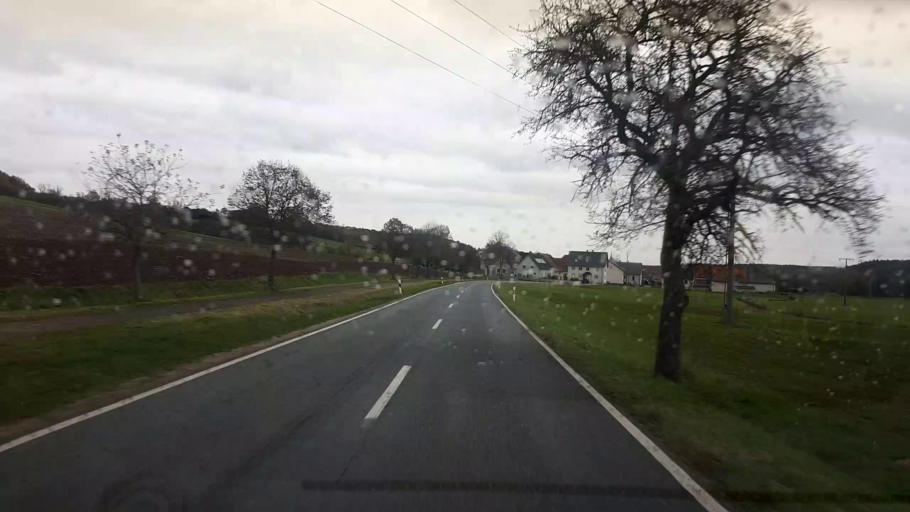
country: DE
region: Bavaria
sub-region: Upper Franconia
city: Burgwindheim
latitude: 49.8717
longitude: 10.6321
